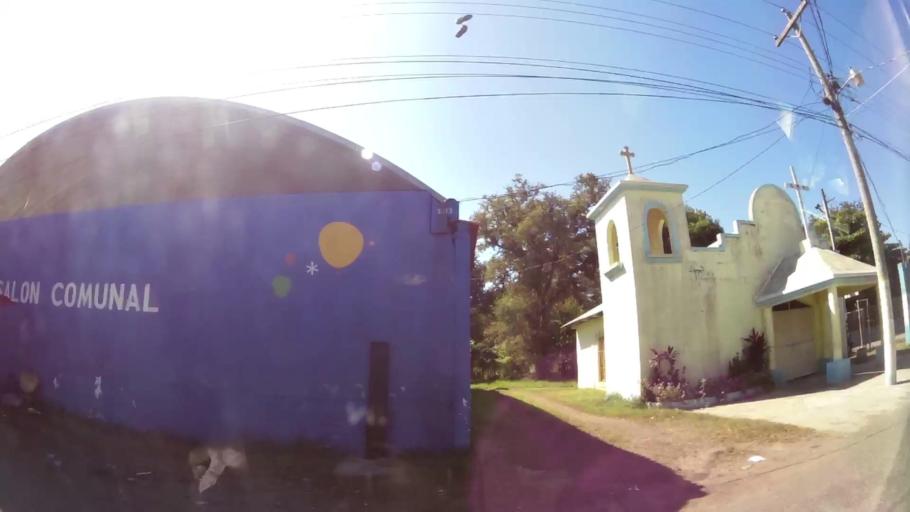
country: GT
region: Escuintla
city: Iztapa
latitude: 13.9233
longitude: -90.5770
